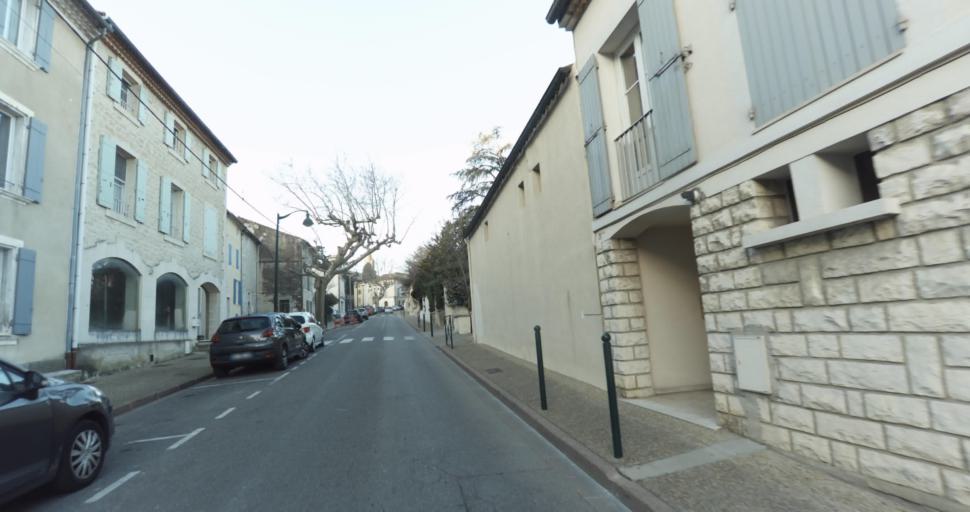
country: FR
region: Provence-Alpes-Cote d'Azur
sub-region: Departement des Bouches-du-Rhone
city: Barbentane
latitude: 43.8996
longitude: 4.7510
